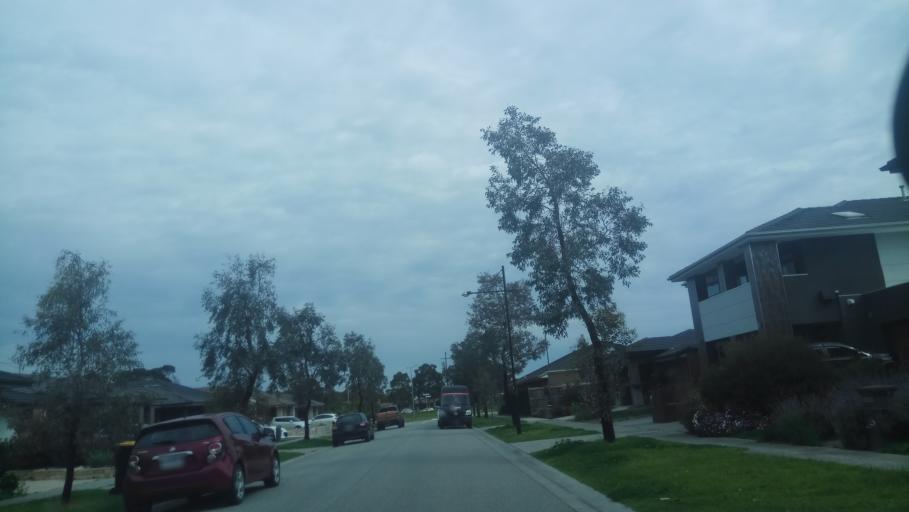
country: AU
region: Victoria
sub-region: Greater Dandenong
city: Keysborough
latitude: -38.0100
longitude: 145.1708
